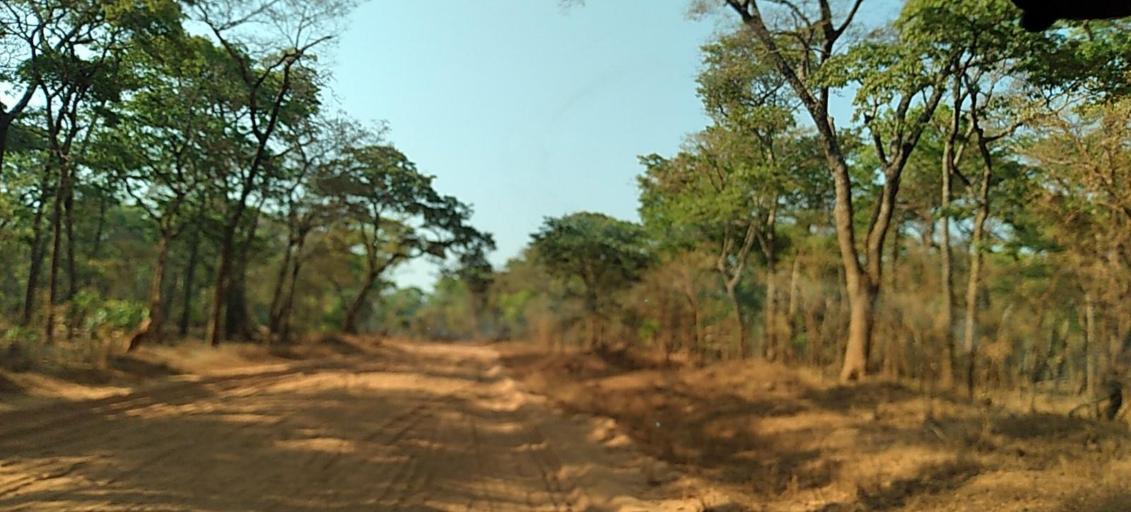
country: ZM
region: North-Western
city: Kasempa
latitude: -13.6155
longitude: 25.9792
